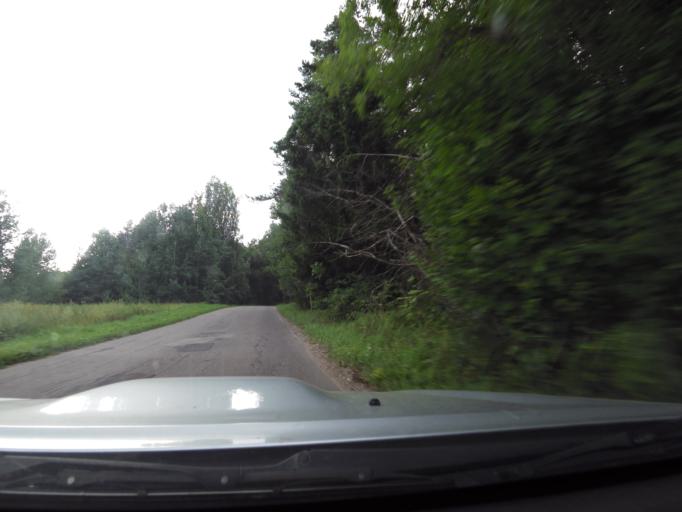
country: LT
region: Siauliu apskritis
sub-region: Siauliai
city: Siauliai
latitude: 55.8565
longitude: 23.1250
